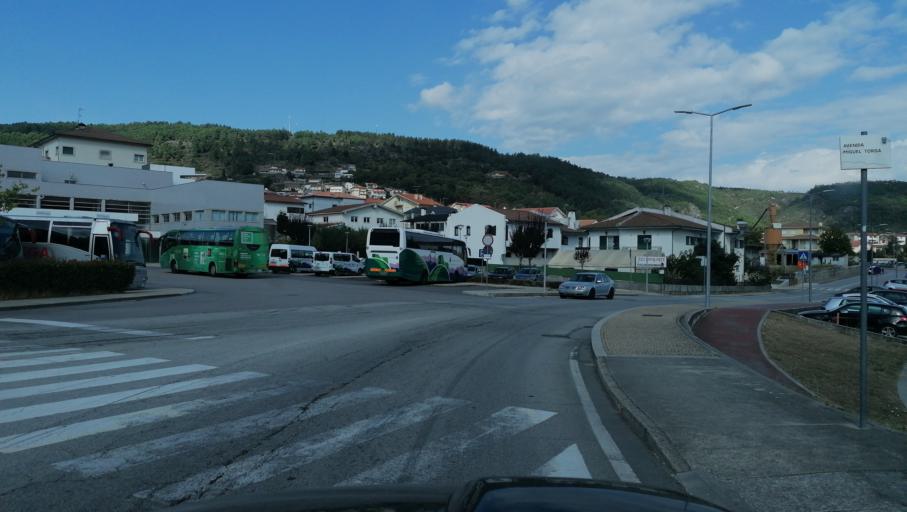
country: PT
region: Vila Real
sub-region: Vila Pouca de Aguiar
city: Vila Pouca de Aguiar
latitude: 41.5020
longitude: -7.6403
